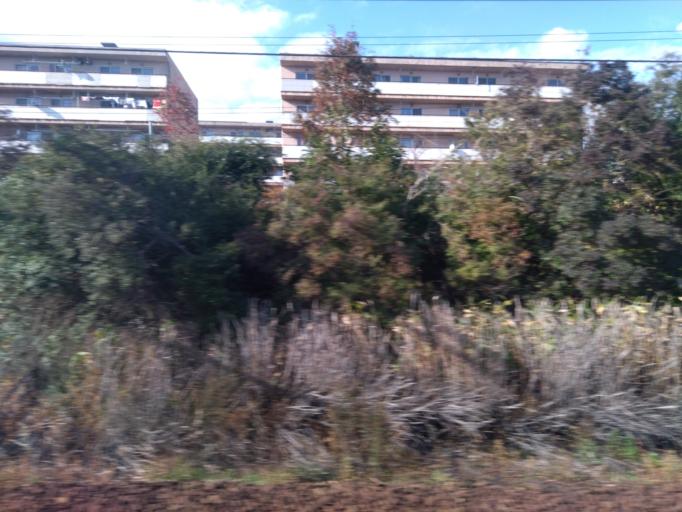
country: JP
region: Hokkaido
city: Muroran
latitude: 42.3582
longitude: 141.0392
